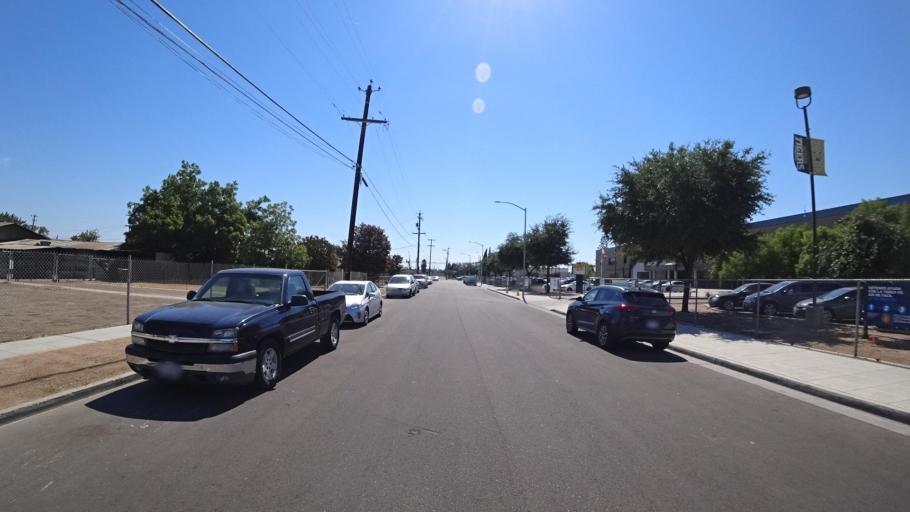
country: US
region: California
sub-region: Fresno County
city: Fresno
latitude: 36.7268
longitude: -119.7562
